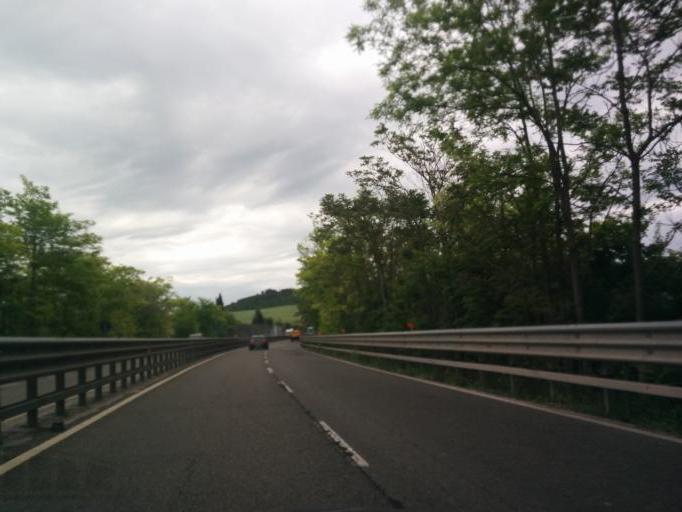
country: IT
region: Tuscany
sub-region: Provincia di Siena
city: Monteriggioni
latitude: 43.3892
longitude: 11.2682
